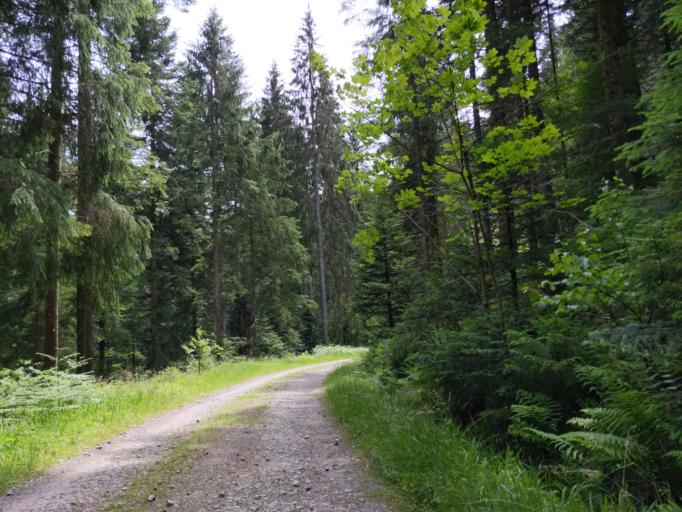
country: DE
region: Baden-Wuerttemberg
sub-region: Karlsruhe Region
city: Freudenstadt
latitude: 48.4395
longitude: 8.3704
